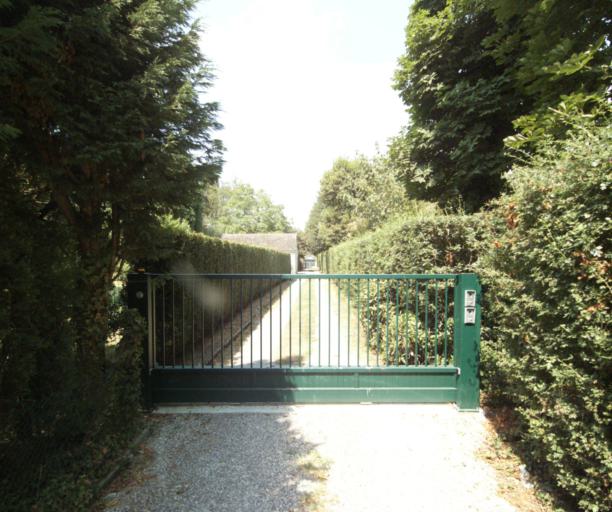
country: FR
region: Nord-Pas-de-Calais
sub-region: Departement du Nord
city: Wervicq-Sud
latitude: 50.7672
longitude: 3.0286
